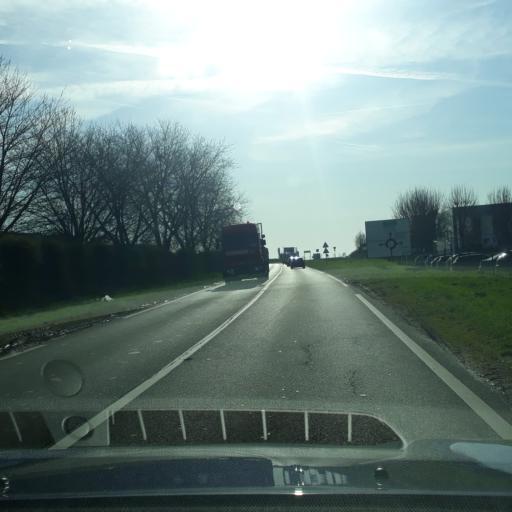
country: FR
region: Ile-de-France
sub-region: Departement de l'Essonne
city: Corbreuse
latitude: 48.4532
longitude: 1.9234
